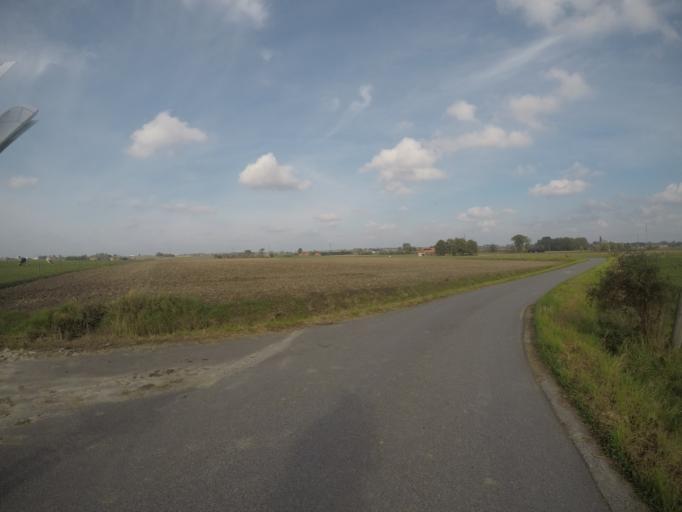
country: BE
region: Flanders
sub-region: Provincie West-Vlaanderen
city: Moorslede
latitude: 50.8443
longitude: 3.0594
